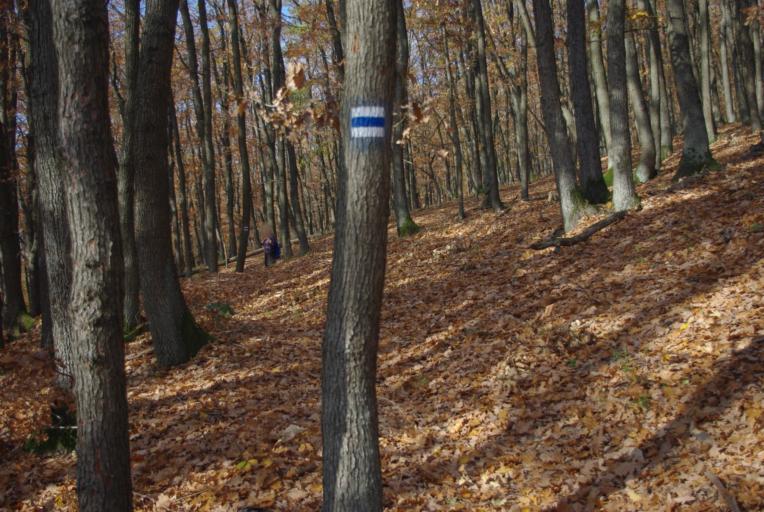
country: HU
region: Borsod-Abauj-Zemplen
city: Satoraljaujhely
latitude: 48.3890
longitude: 21.5920
